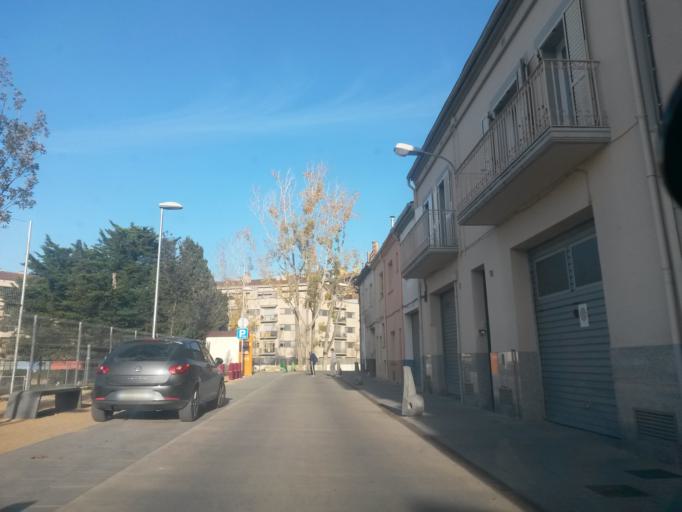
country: ES
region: Catalonia
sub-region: Provincia de Girona
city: Banyoles
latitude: 42.1200
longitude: 2.7623
